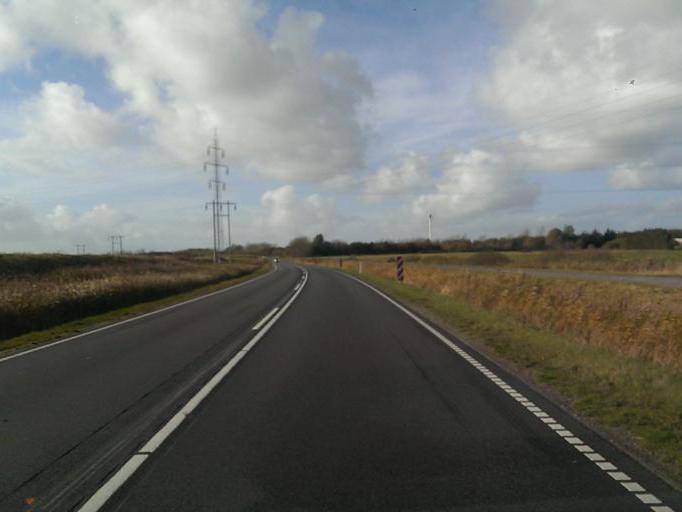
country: DK
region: South Denmark
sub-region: Esbjerg Kommune
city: Tjaereborg
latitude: 55.4660
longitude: 8.5356
